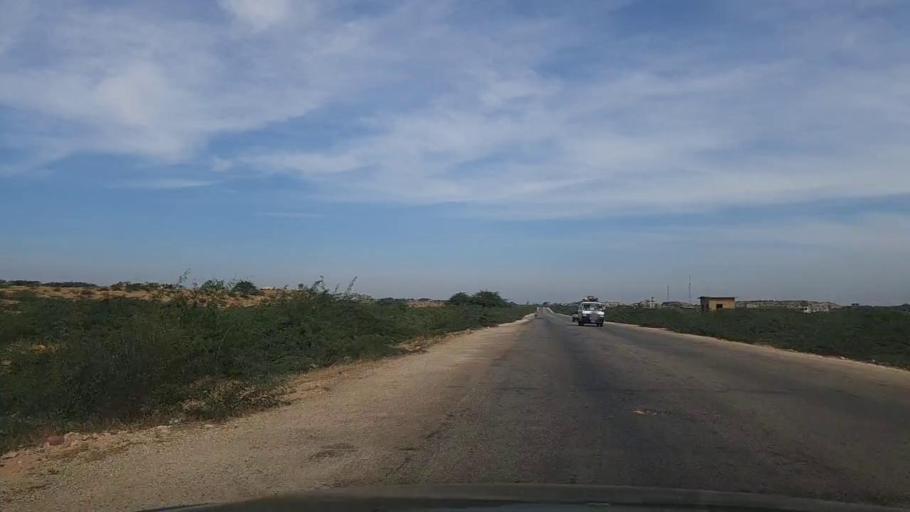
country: PK
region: Sindh
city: Daro Mehar
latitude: 24.8841
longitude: 68.0548
